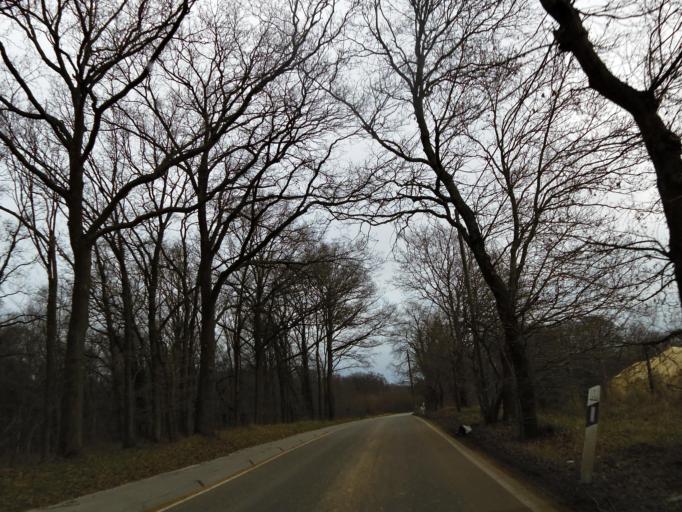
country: NL
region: Limburg
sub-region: Gemeente Onderbanken
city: Schinveld
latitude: 50.9582
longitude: 6.0067
